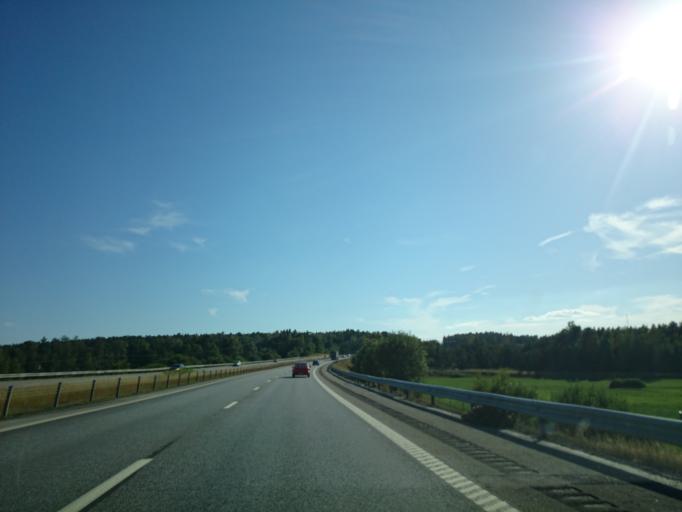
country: SE
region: Soedermanland
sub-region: Trosa Kommun
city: Vagnharad
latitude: 58.9369
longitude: 17.4253
